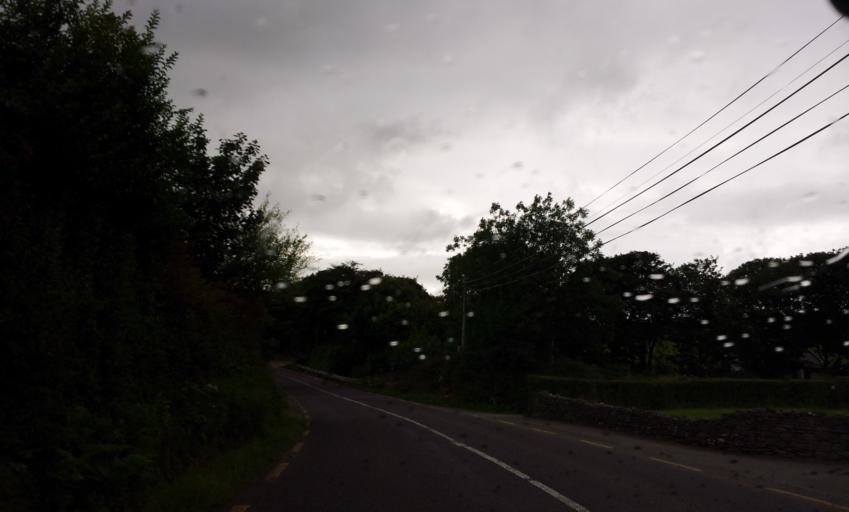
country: IE
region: Munster
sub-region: Ciarrai
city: Killorglin
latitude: 52.1803
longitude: -9.9727
